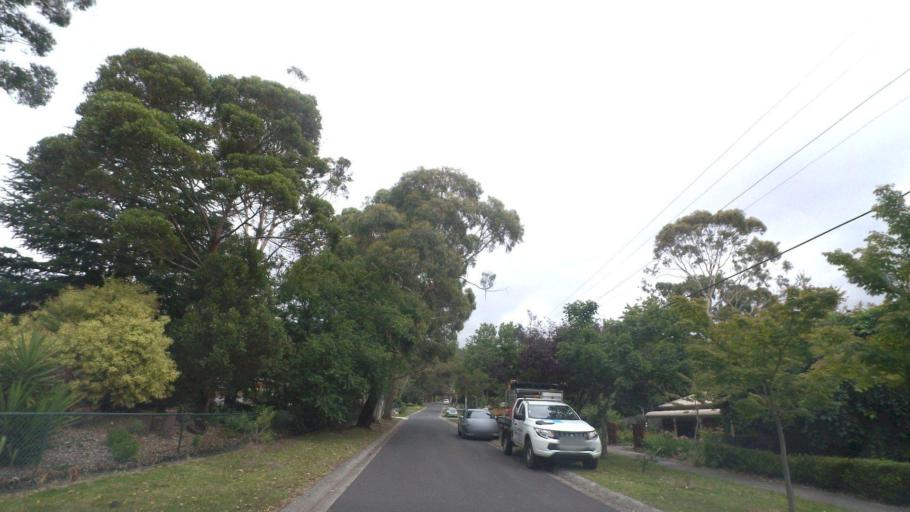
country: AU
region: Victoria
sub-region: Knox
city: The Basin
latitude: -37.8576
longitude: 145.3065
